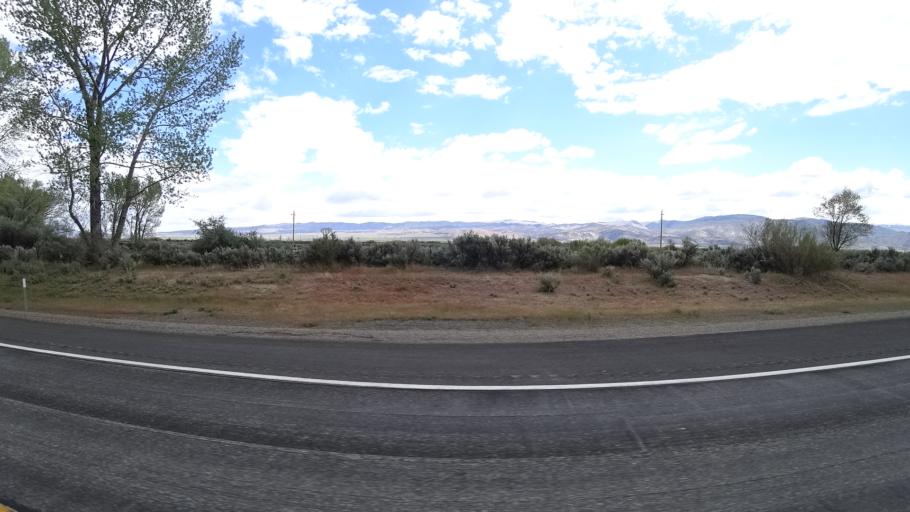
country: US
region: Nevada
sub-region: Lyon County
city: Smith Valley
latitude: 38.6077
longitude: -119.5200
